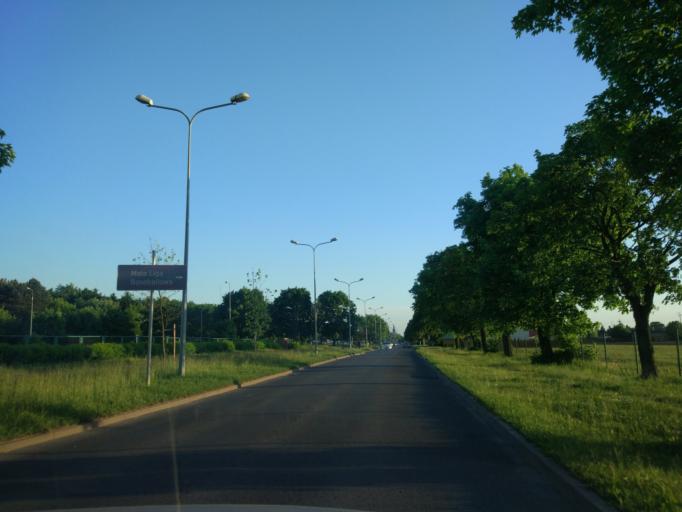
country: PL
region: Lodz Voivodeship
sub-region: Powiat kutnowski
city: Kutno
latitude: 52.2438
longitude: 19.3758
